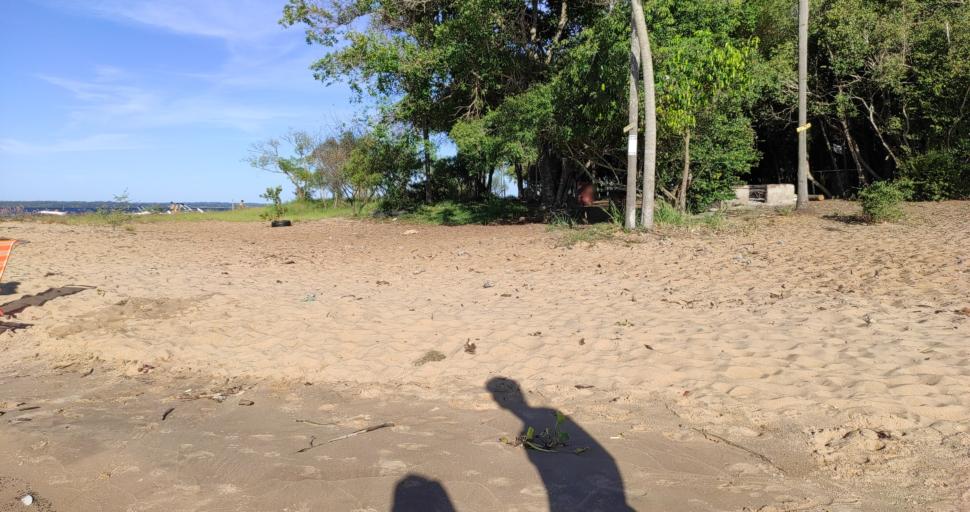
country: PY
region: Itapua
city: San Juan del Parana
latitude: -27.3400
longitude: -55.9510
